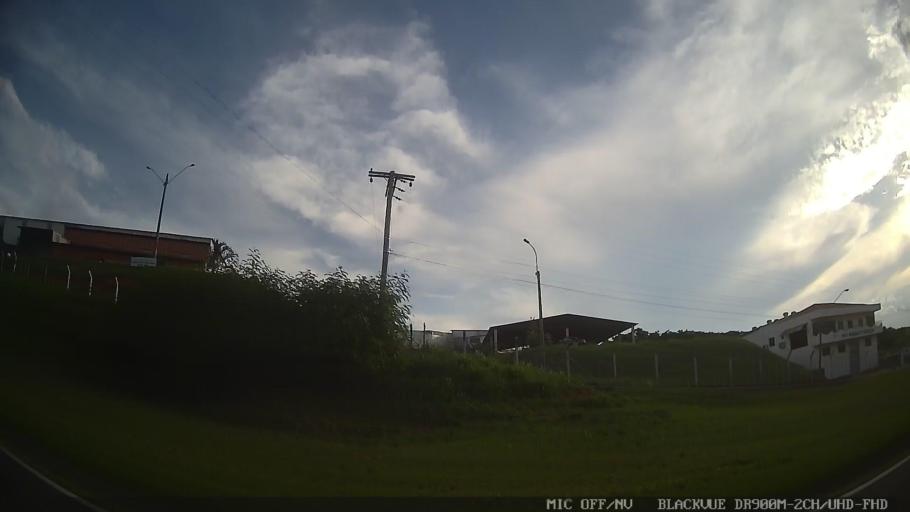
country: BR
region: Sao Paulo
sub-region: Tiete
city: Tiete
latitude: -23.1186
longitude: -47.7133
